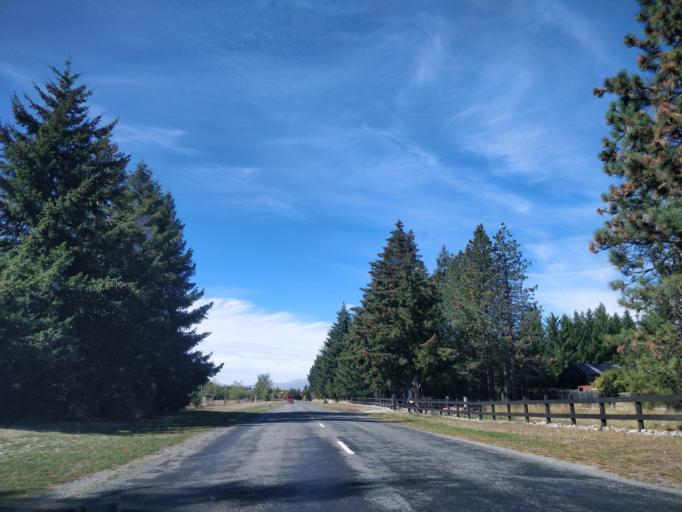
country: NZ
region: Canterbury
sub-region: Timaru District
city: Pleasant Point
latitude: -44.2444
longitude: 170.0911
